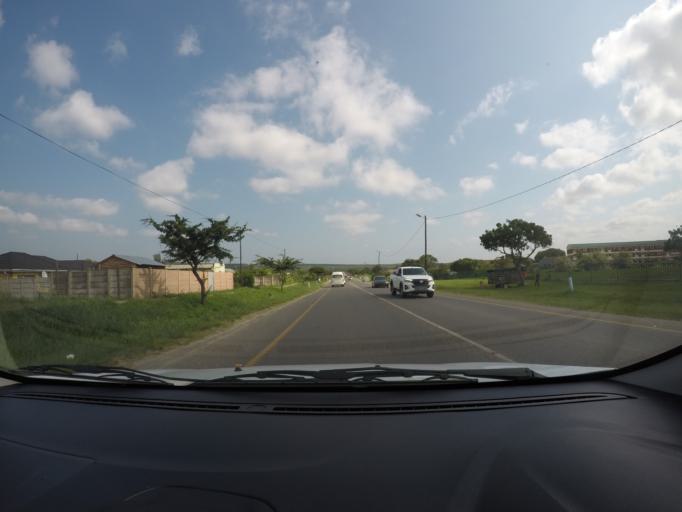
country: ZA
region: KwaZulu-Natal
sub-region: uThungulu District Municipality
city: eSikhawini
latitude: -28.8788
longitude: 31.9024
